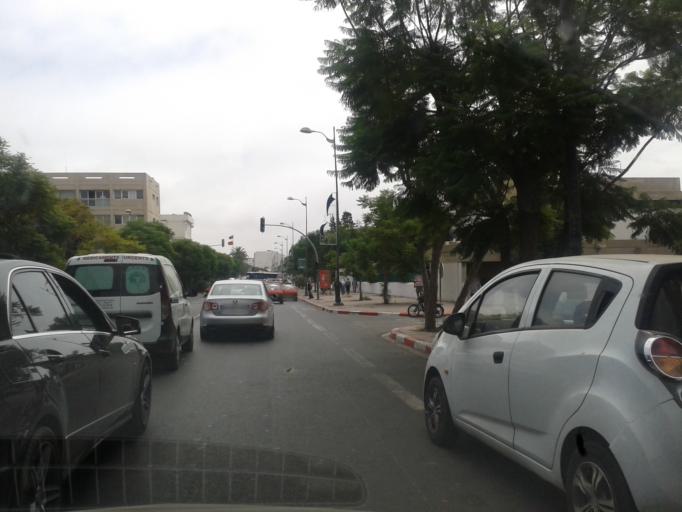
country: MA
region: Souss-Massa-Draa
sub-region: Agadir-Ida-ou-Tnan
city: Agadir
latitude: 30.4225
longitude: -9.6021
